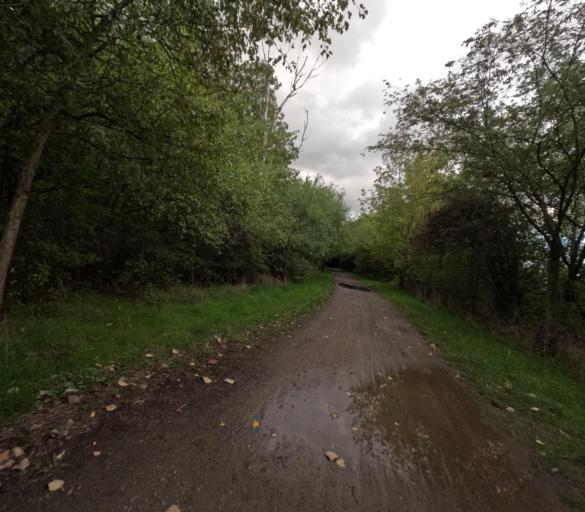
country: DE
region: Saxony
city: Markranstadt
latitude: 51.2947
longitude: 12.2231
